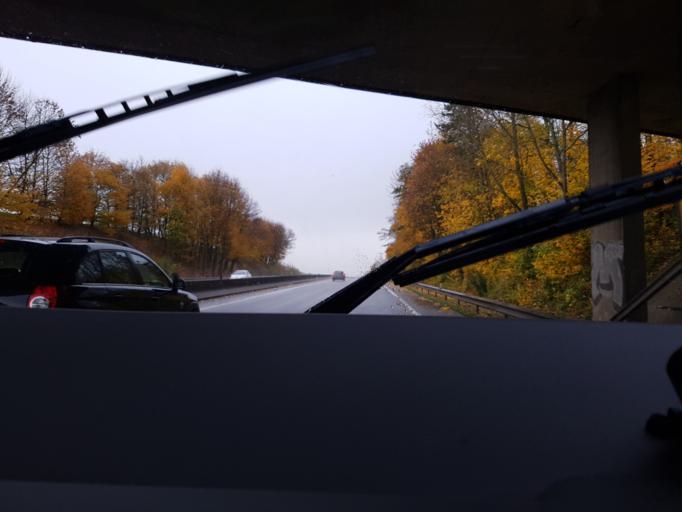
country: FR
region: Nord-Pas-de-Calais
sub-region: Departement du Pas-de-Calais
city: Bully-les-Mines
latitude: 50.4351
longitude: 2.7291
